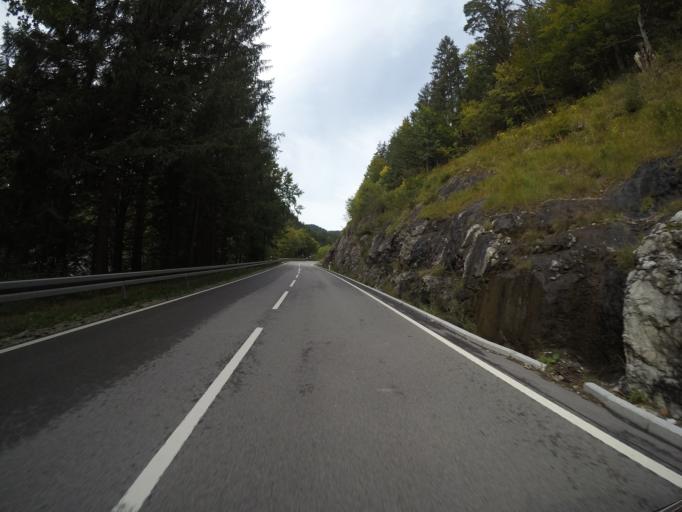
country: DE
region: Bavaria
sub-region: Upper Bavaria
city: Lenggries
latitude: 47.5852
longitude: 11.5541
